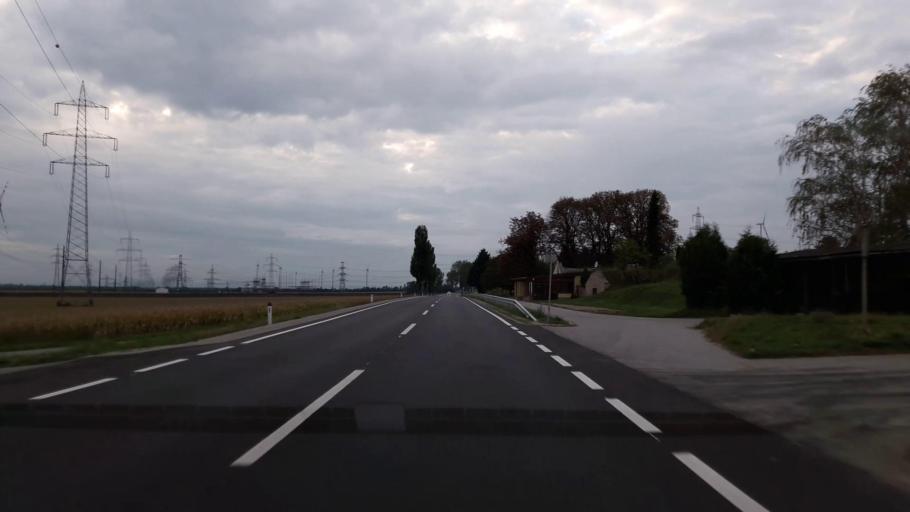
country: AT
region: Lower Austria
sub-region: Politischer Bezirk Bruck an der Leitha
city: Bruck an der Leitha
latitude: 48.0312
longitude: 16.7126
